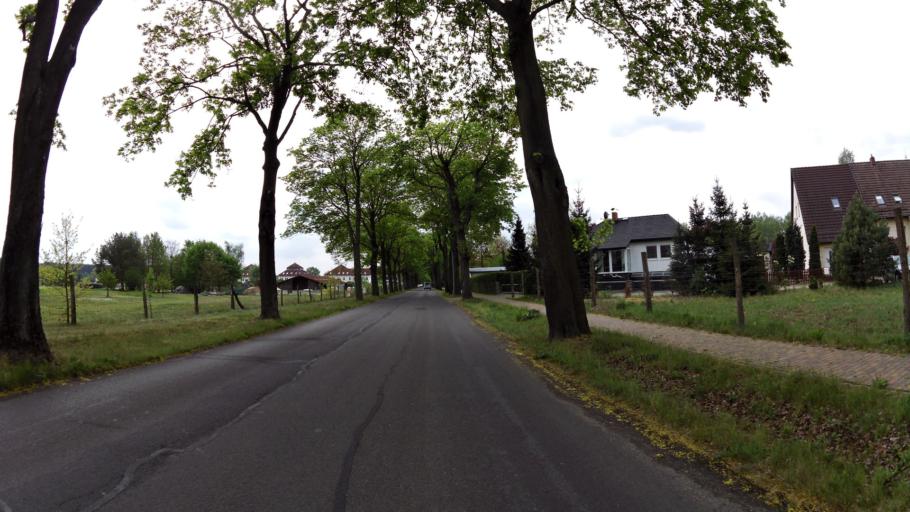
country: DE
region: Brandenburg
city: Bestensee
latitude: 52.2091
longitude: 13.5912
